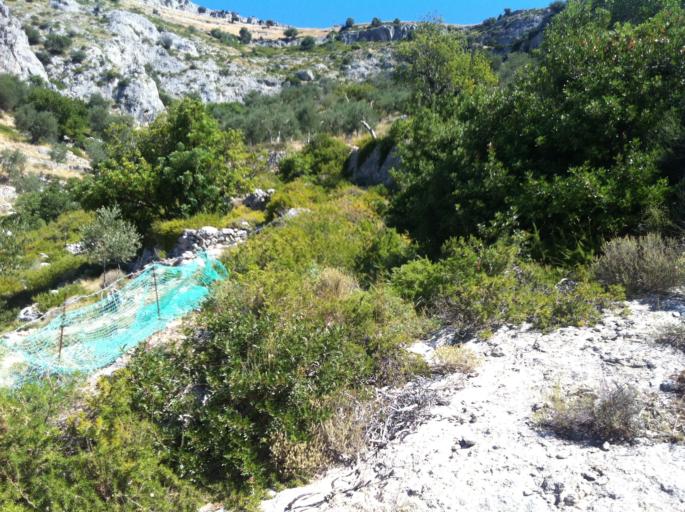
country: IT
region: Apulia
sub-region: Provincia di Foggia
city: Manfredonia
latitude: 41.6654
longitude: 15.9175
